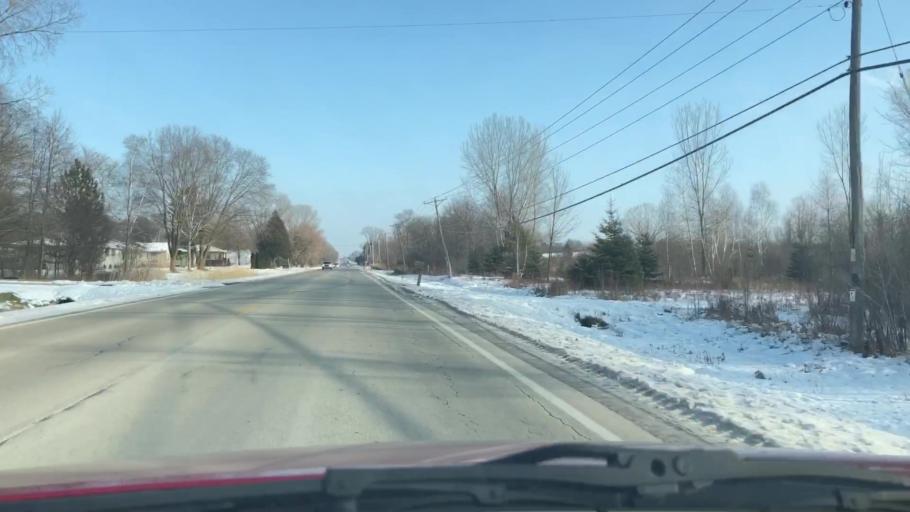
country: US
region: Wisconsin
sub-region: Outagamie County
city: Appleton
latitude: 44.3167
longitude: -88.4282
